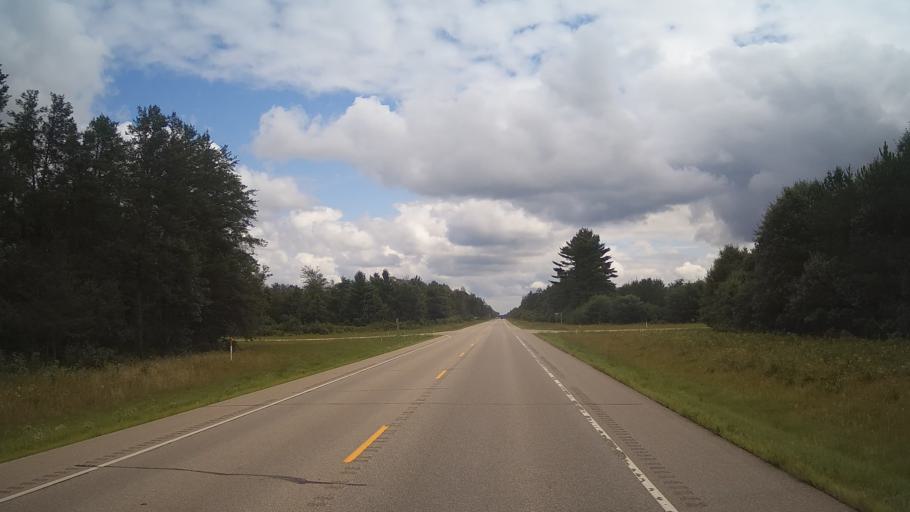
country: US
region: Wisconsin
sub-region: Adams County
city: Friendship
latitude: 44.0251
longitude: -89.7495
